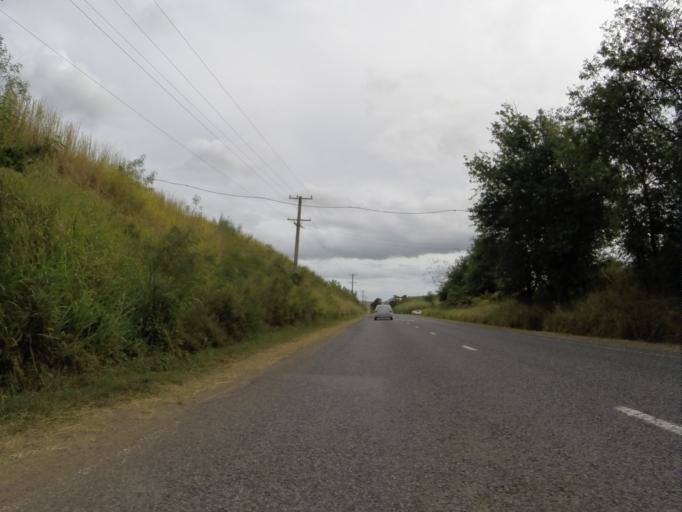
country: FJ
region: Western
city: Nadi
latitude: -18.0466
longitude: 177.3427
